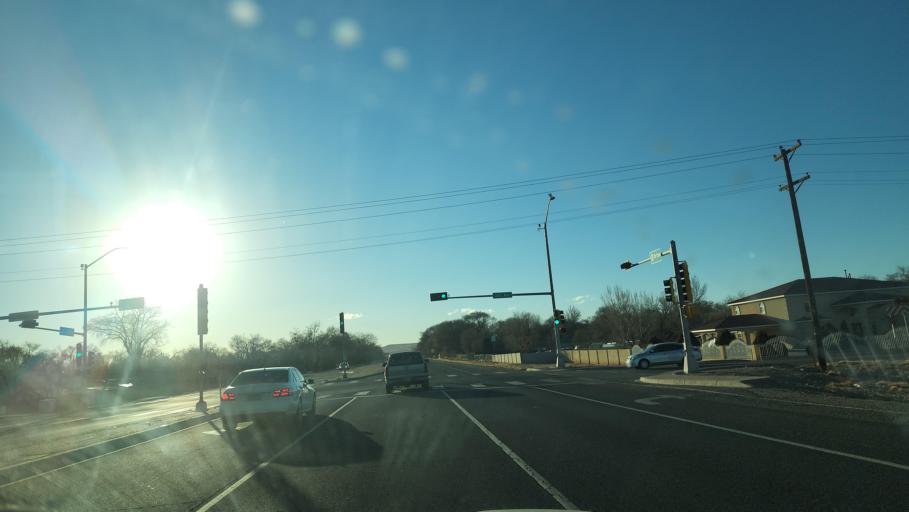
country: US
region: New Mexico
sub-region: Bernalillo County
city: South Valley
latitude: 35.0269
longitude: -106.6894
